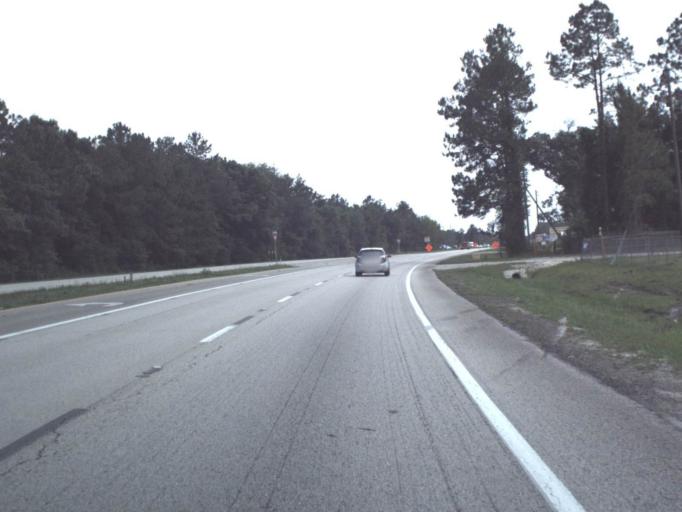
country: US
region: Florida
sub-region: Bradford County
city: Starke
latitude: 30.0609
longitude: -82.0662
